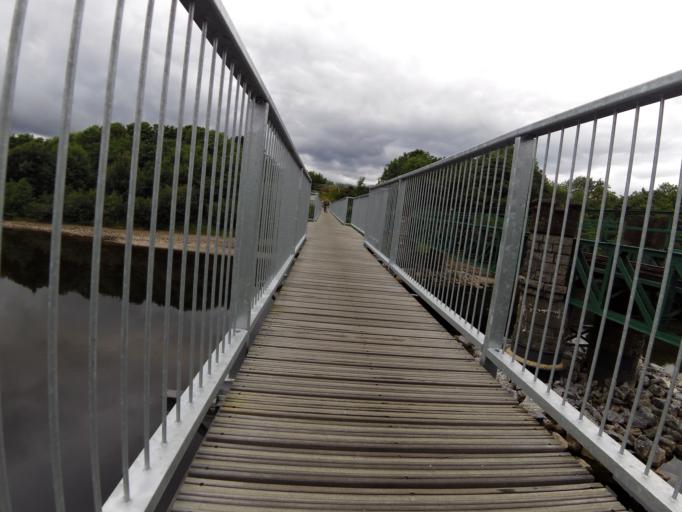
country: GB
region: Scotland
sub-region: Highland
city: Fort William
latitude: 56.8329
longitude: -5.0840
